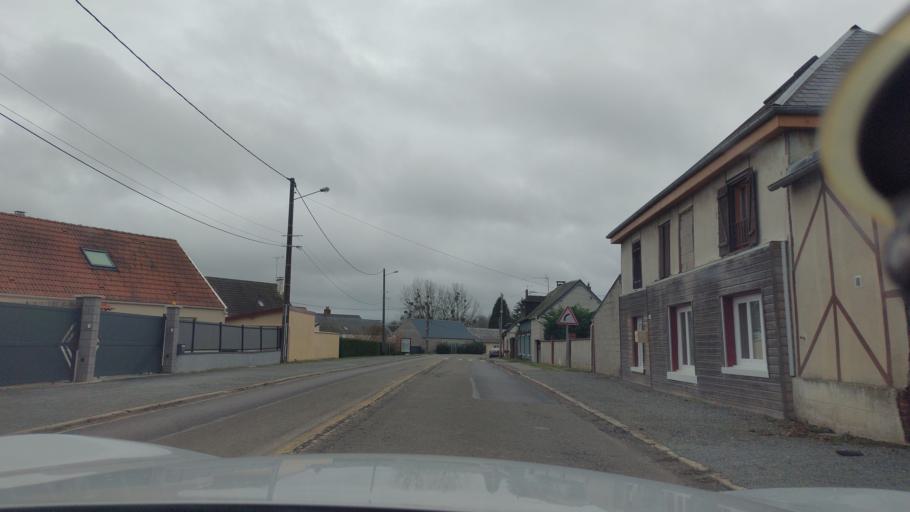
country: FR
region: Picardie
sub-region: Departement de l'Oise
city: Grandvilliers
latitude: 49.6344
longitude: 1.9465
